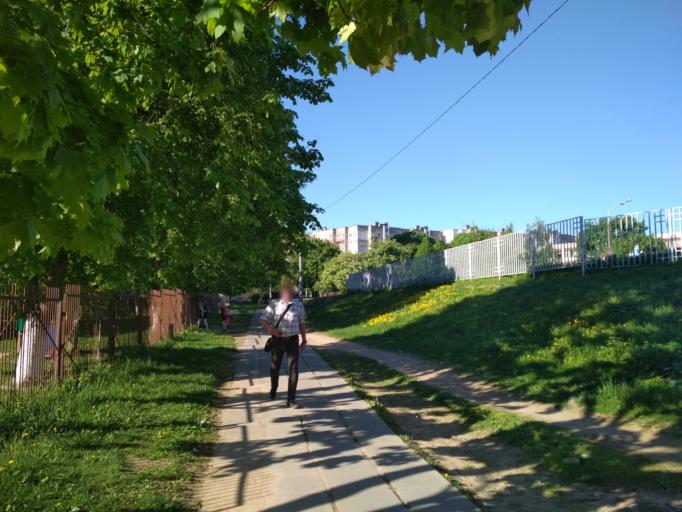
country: BY
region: Minsk
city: Minsk
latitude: 53.8815
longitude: 27.5458
